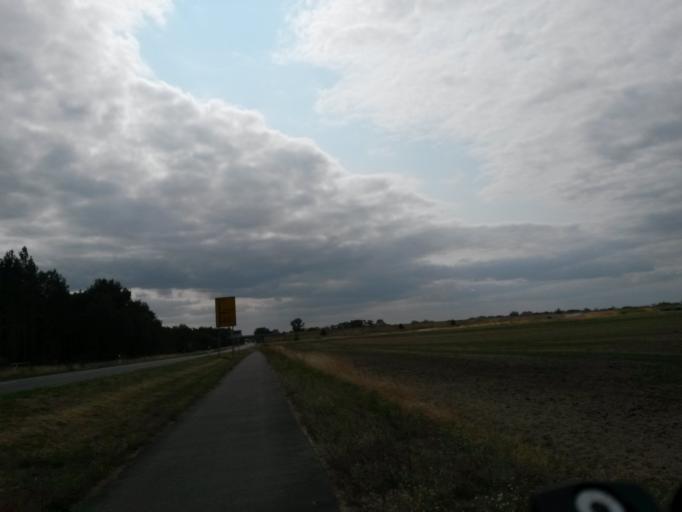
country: DE
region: Saxony-Anhalt
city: Schonhausen
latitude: 52.5543
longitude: 12.0258
